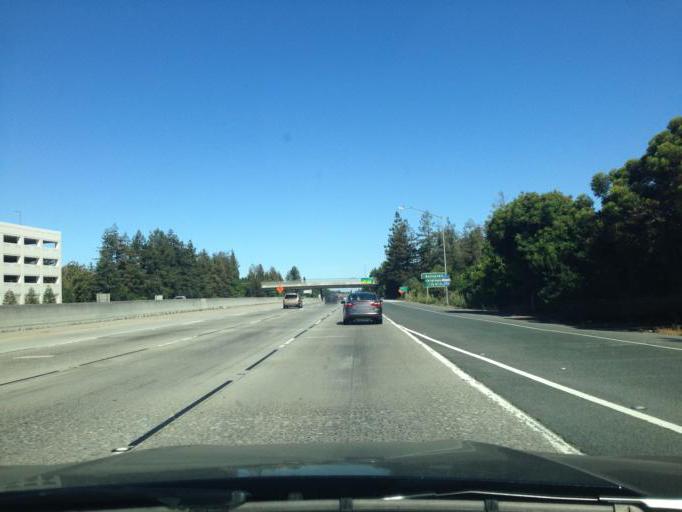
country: US
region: California
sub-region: Santa Clara County
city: Cupertino
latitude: 37.3249
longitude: -122.0031
